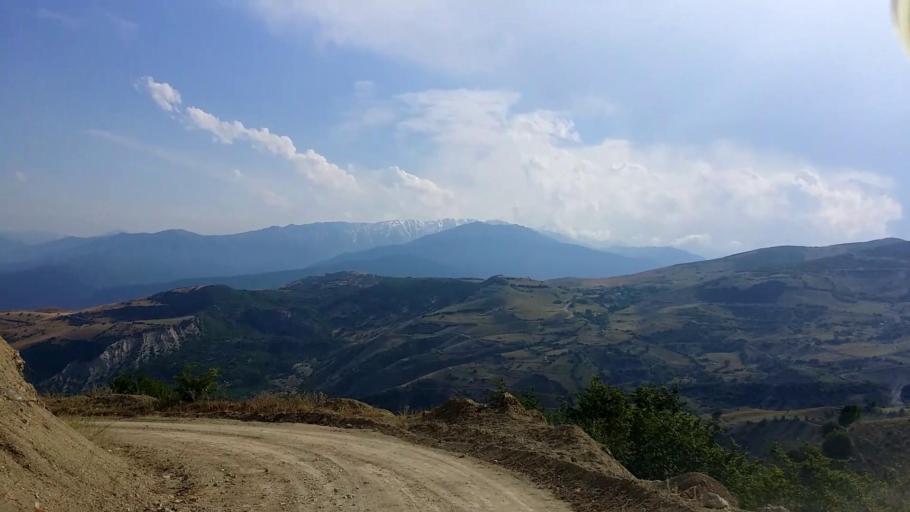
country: IR
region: Mazandaran
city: Chalus
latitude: 36.5516
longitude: 51.2947
